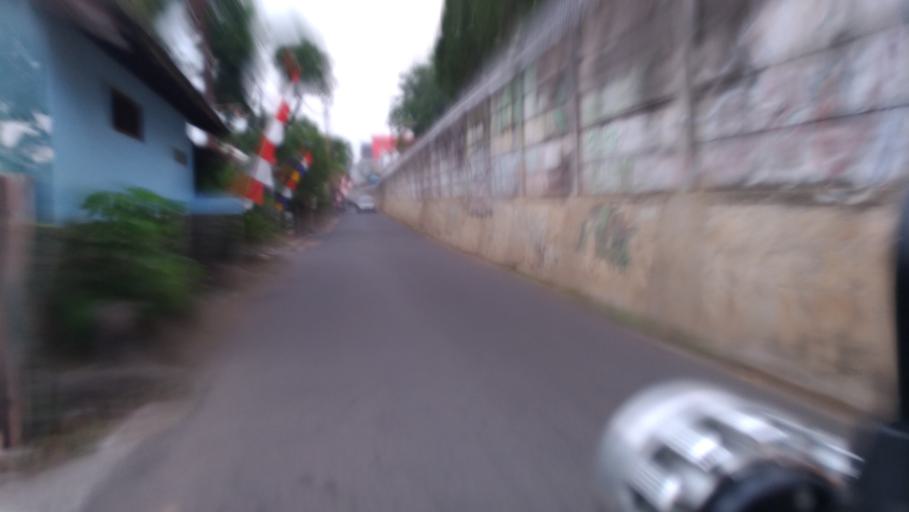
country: ID
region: West Java
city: Depok
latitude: -6.3471
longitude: 106.8687
